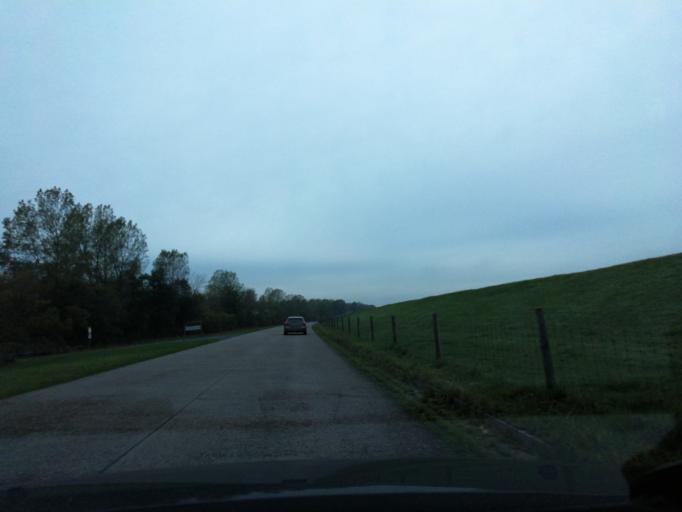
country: DE
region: Lower Saxony
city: Schillig
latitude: 53.6393
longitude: 8.0503
